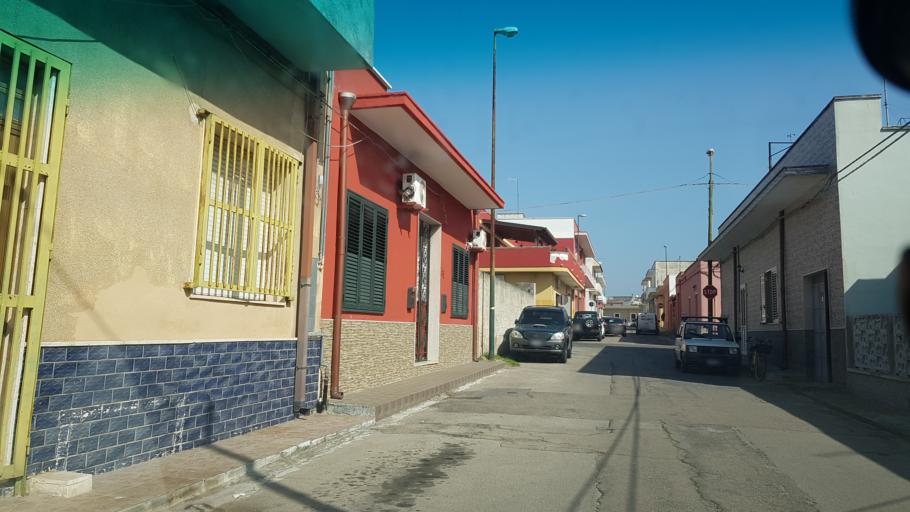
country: IT
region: Apulia
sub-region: Provincia di Brindisi
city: Torchiarolo
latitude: 40.4839
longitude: 18.0496
